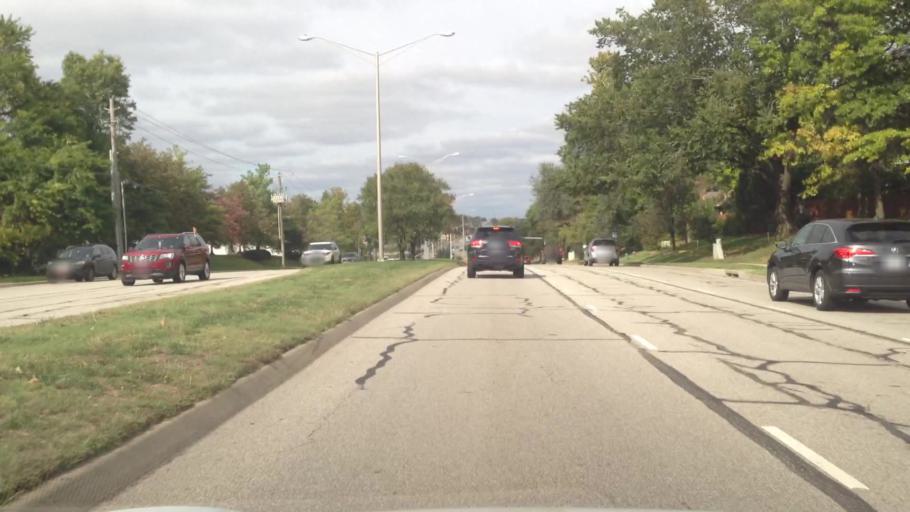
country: US
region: Kansas
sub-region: Johnson County
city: Lenexa
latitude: 38.9306
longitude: -94.7234
